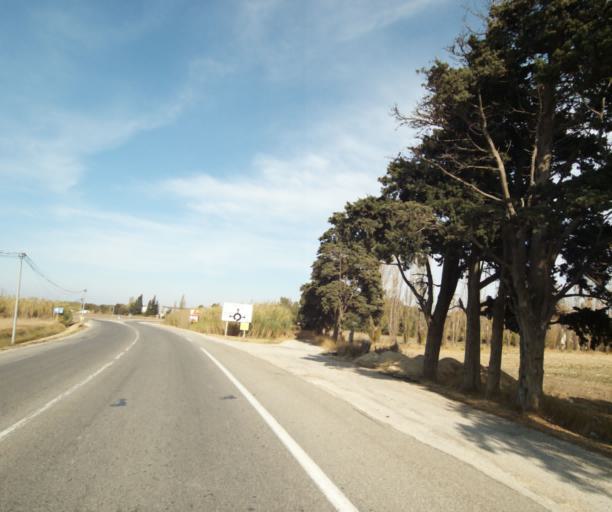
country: FR
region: Provence-Alpes-Cote d'Azur
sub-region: Departement des Bouches-du-Rhone
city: Chateauneuf-les-Martigues
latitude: 43.3920
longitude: 5.1939
